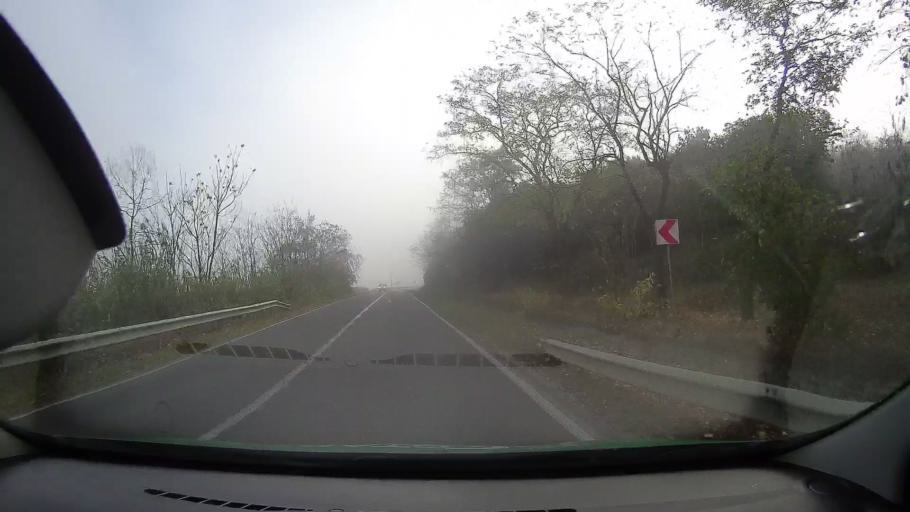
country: RO
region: Tulcea
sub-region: Municipiul Tulcea
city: Tulcea
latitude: 45.1670
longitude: 28.8384
